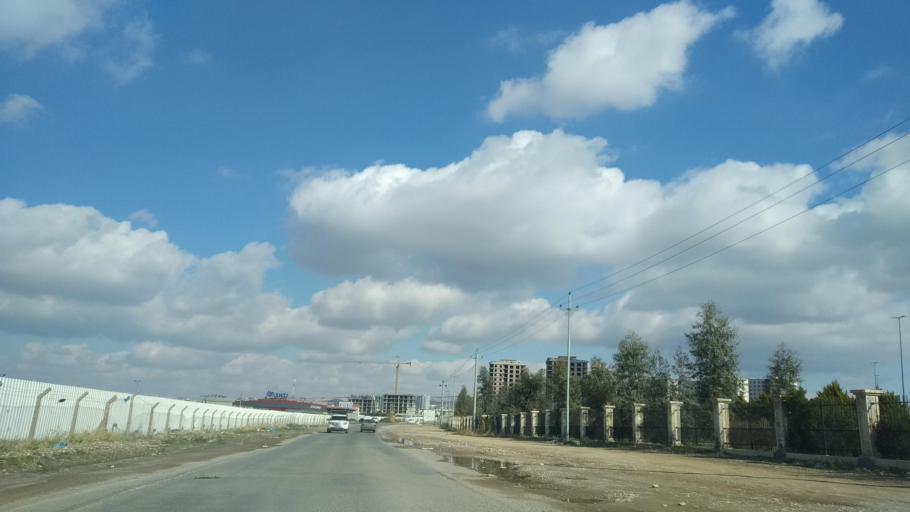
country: IQ
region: Arbil
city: Erbil
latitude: 36.2107
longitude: 44.1346
